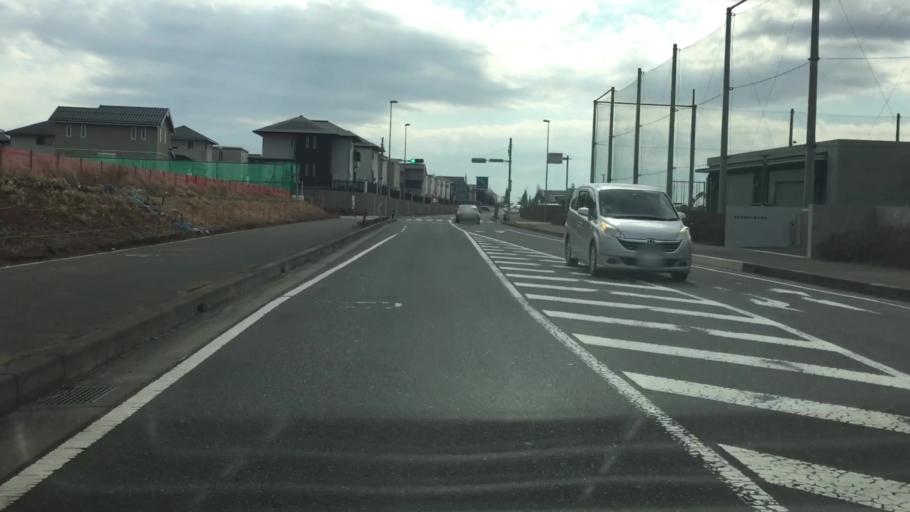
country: JP
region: Ibaraki
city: Ryugasaki
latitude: 35.8120
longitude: 140.1618
